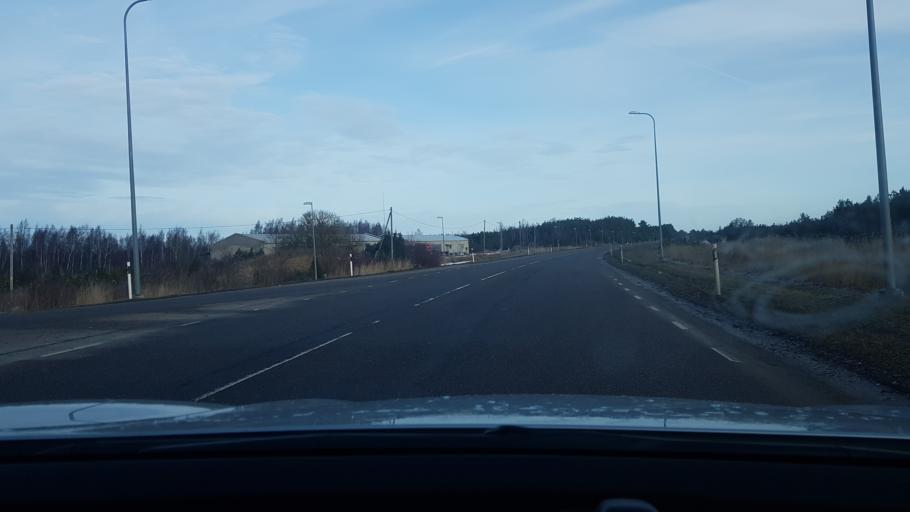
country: EE
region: Saare
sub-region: Kuressaare linn
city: Kuressaare
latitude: 58.2368
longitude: 22.5003
